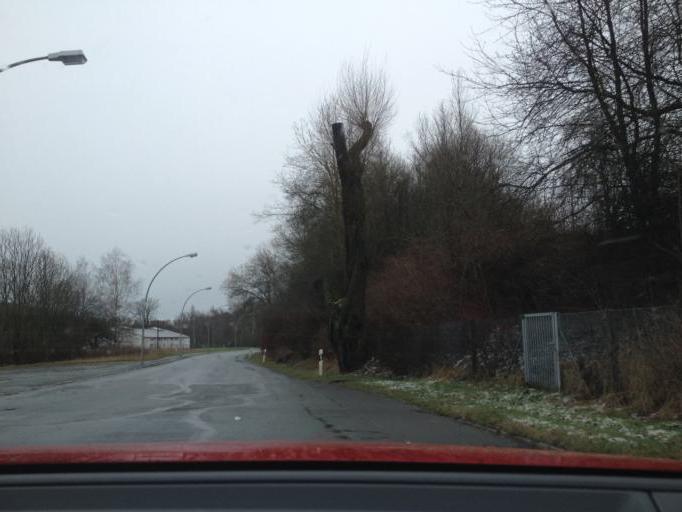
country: DE
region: Bavaria
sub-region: Upper Franconia
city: Hof
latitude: 50.3071
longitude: 11.9307
